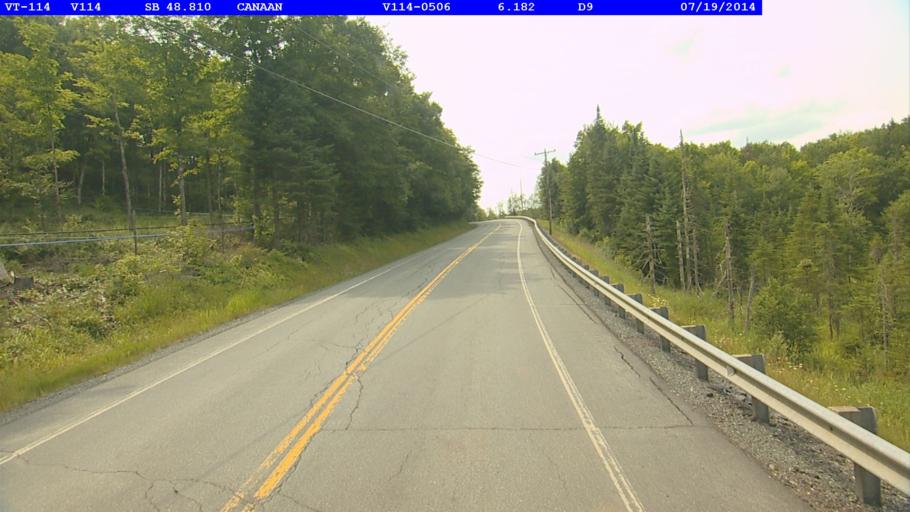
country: US
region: New Hampshire
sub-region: Coos County
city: Colebrook
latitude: 45.0088
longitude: -71.5721
